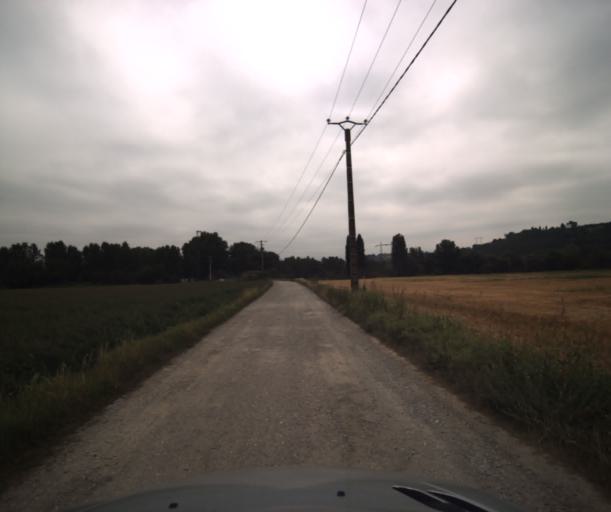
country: FR
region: Midi-Pyrenees
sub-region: Departement de la Haute-Garonne
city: Vieille-Toulouse
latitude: 43.5367
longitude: 1.4249
